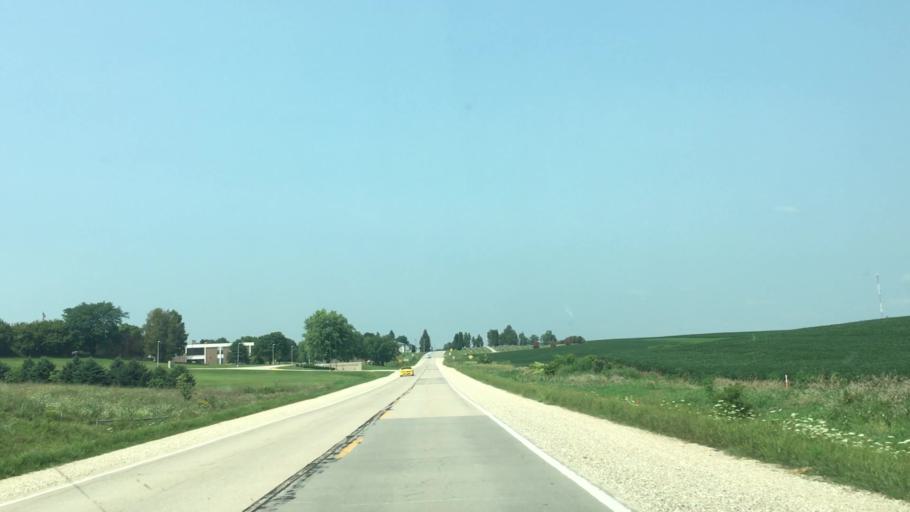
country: US
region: Iowa
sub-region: Winneshiek County
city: Decorah
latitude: 43.1715
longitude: -91.8644
